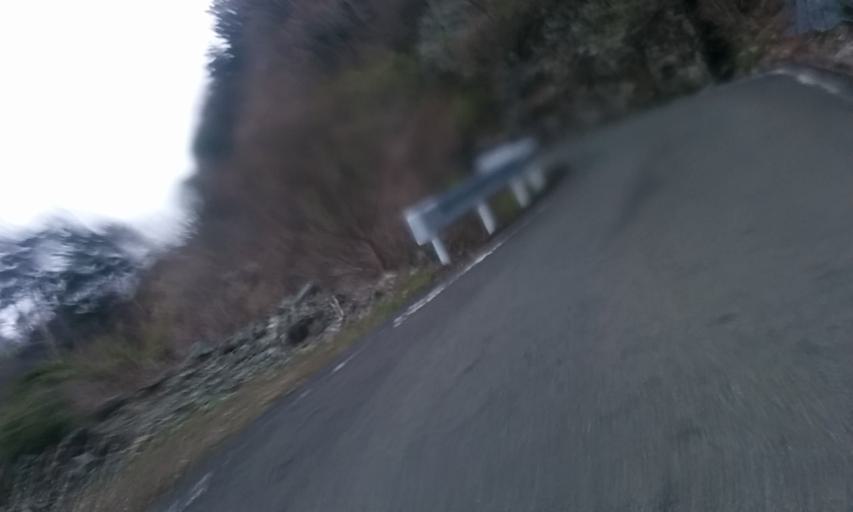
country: JP
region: Ehime
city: Saijo
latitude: 33.7805
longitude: 133.2374
